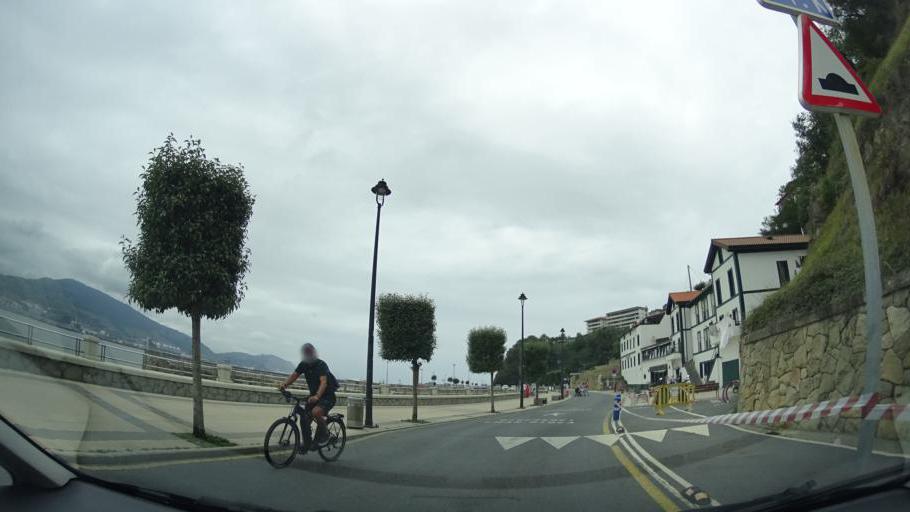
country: ES
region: Basque Country
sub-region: Bizkaia
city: Algorta
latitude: 43.3486
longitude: -3.0142
